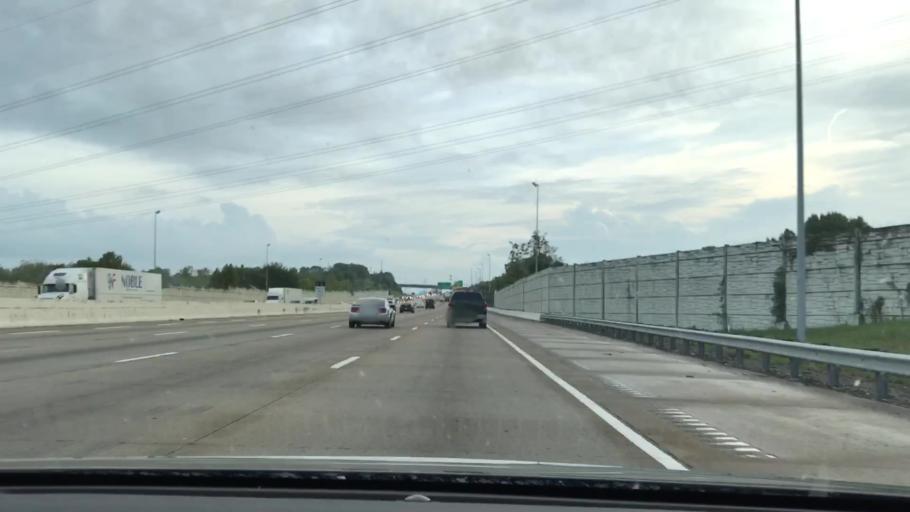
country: US
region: Tennessee
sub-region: Davidson County
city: Goodlettsville
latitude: 36.2920
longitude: -86.7205
